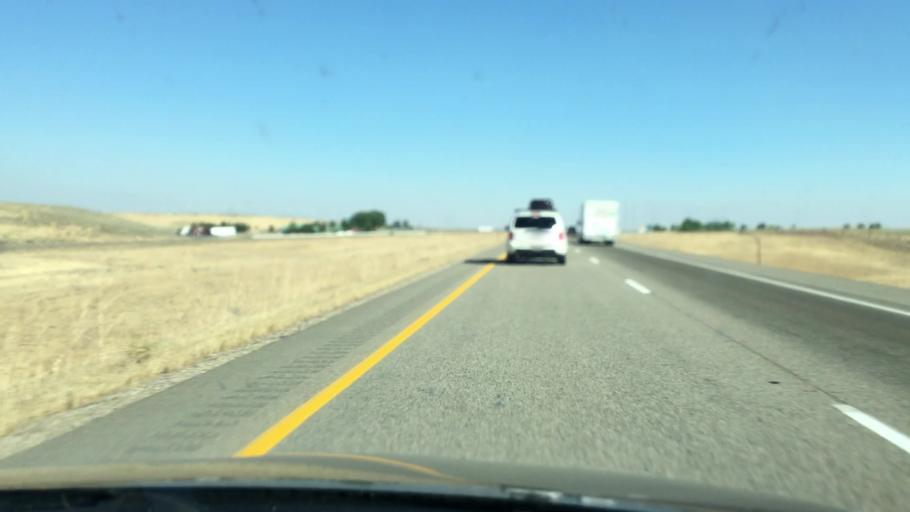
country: US
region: Idaho
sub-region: Ada County
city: Boise
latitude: 43.4816
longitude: -116.1125
